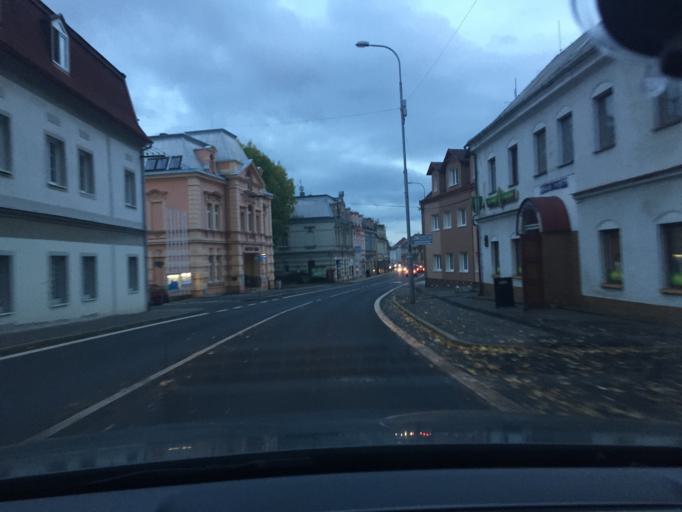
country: CZ
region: Ustecky
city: Dubi
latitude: 50.6770
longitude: 13.7911
